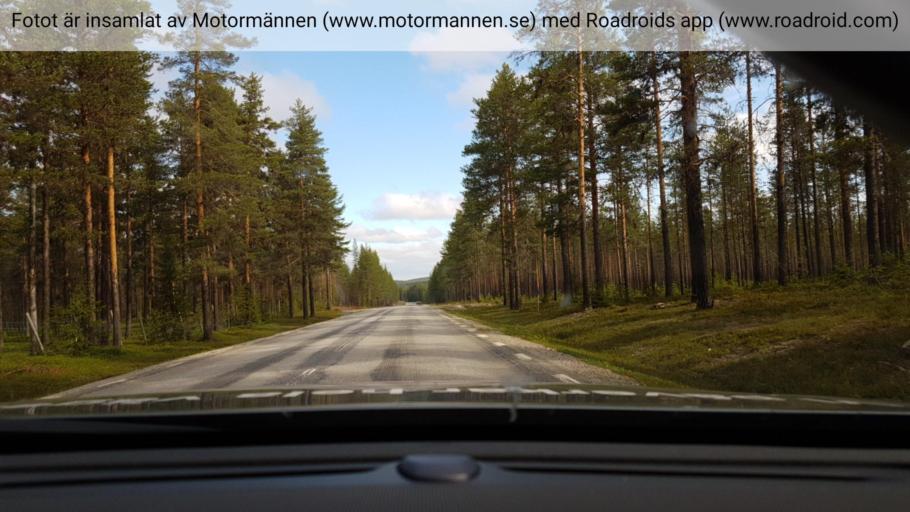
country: SE
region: Vaesterbotten
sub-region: Norsjo Kommun
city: Norsjoe
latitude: 64.7233
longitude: 19.1326
